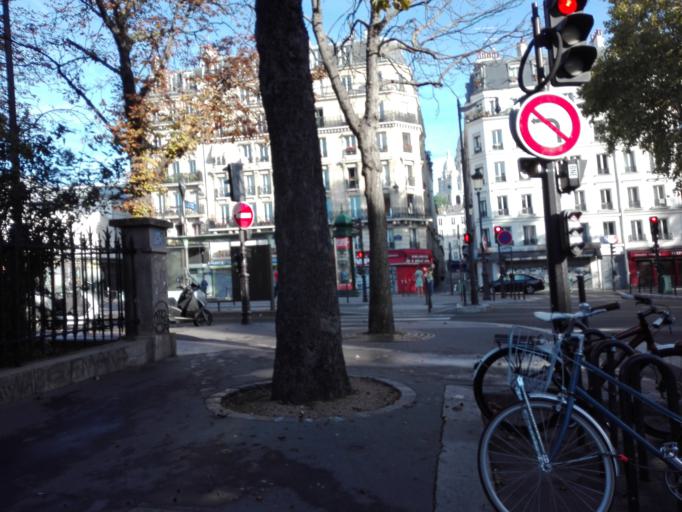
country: FR
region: Ile-de-France
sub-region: Paris
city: Saint-Ouen
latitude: 48.8826
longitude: 2.3445
